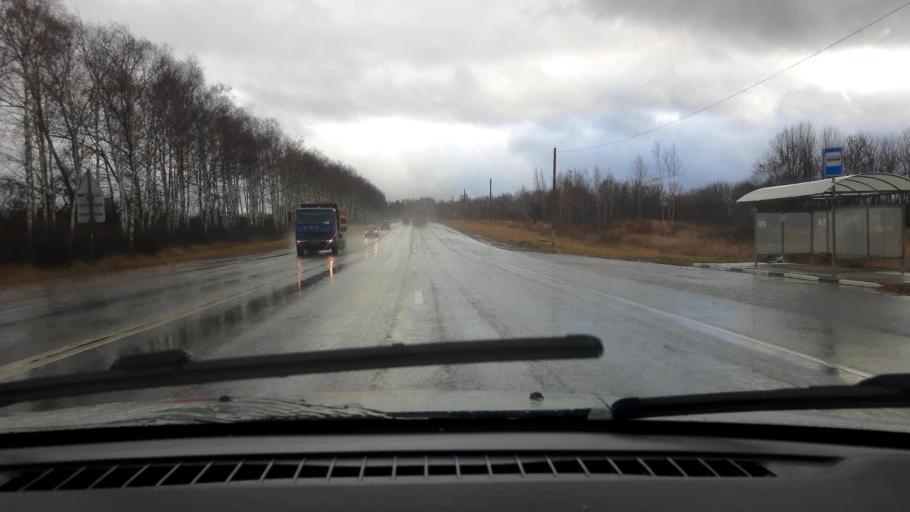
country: RU
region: Nizjnij Novgorod
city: Pamyat' Parizhskoy Kommuny
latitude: 56.0340
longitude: 44.4968
